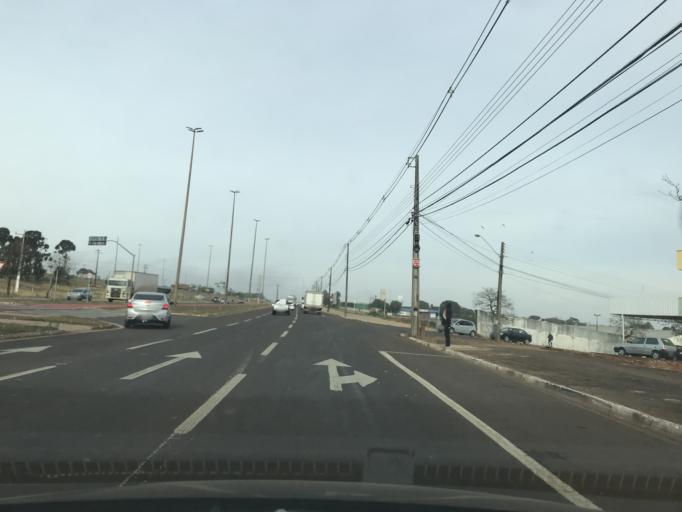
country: BR
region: Parana
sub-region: Cascavel
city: Cascavel
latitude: -24.9775
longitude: -53.4981
